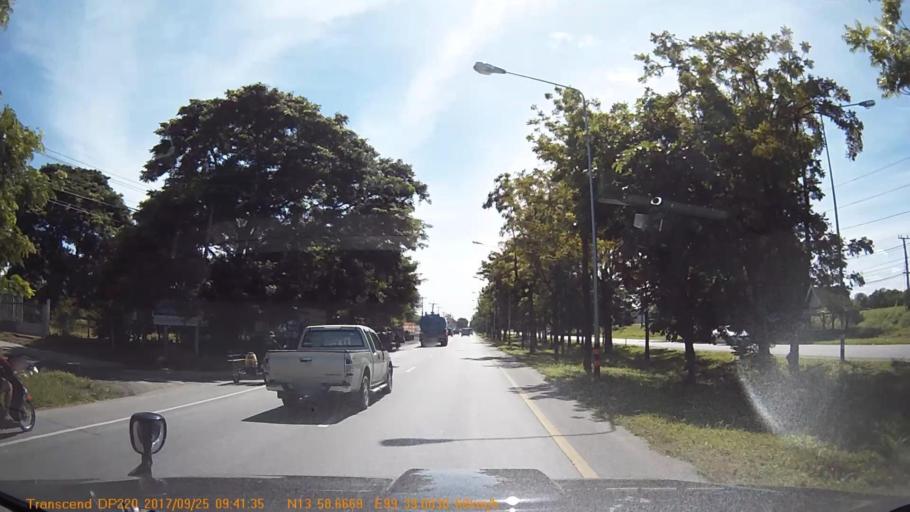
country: TH
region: Kanchanaburi
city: Tha Muang
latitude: 13.9777
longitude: 99.6505
